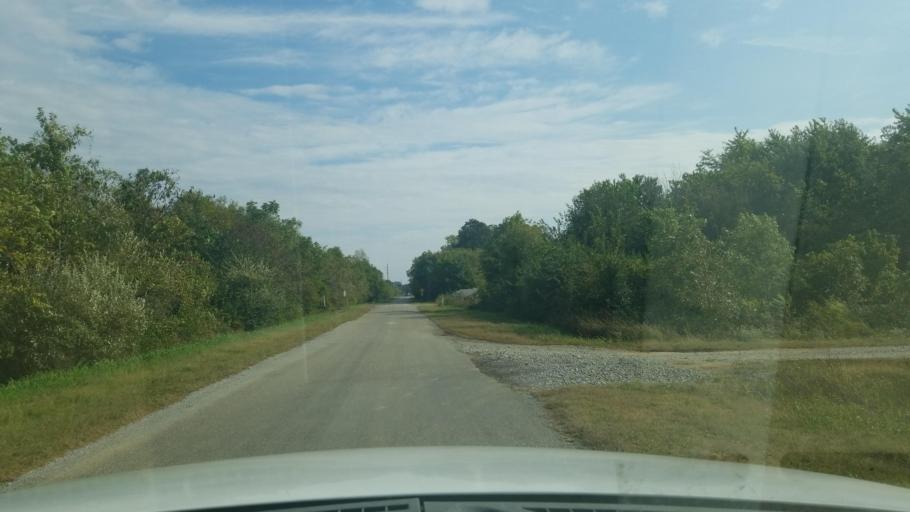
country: US
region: Illinois
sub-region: Saline County
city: Eldorado
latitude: 37.8067
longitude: -88.4491
